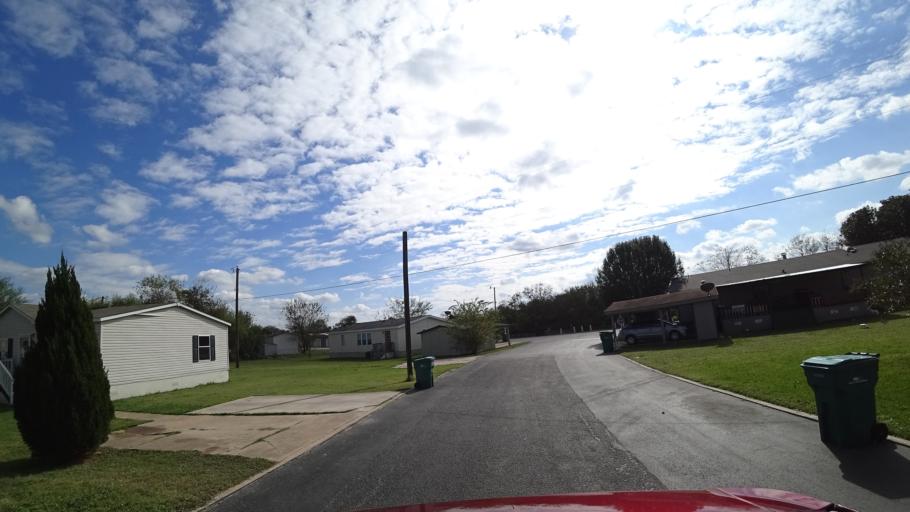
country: US
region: Texas
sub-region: Travis County
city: Pflugerville
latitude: 30.4342
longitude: -97.6446
